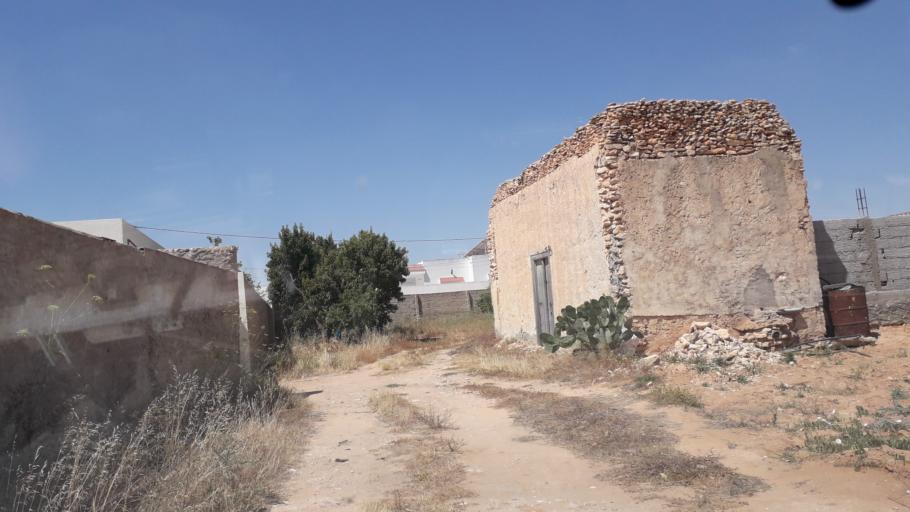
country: TN
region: Safaqis
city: Al Qarmadah
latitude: 34.8211
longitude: 10.7656
